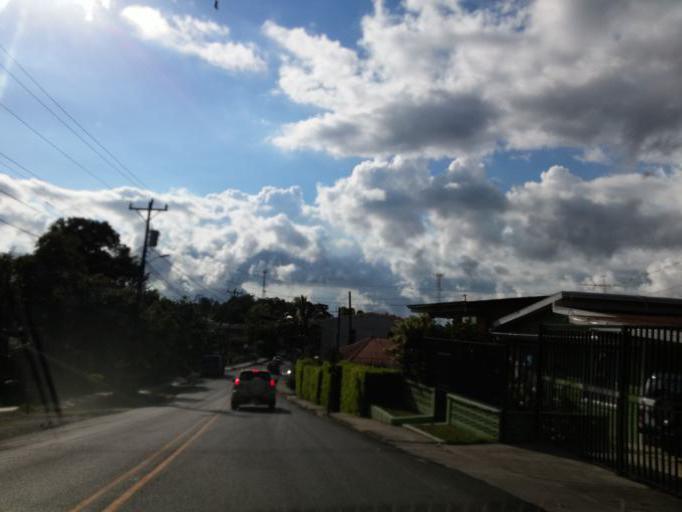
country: CR
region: San Jose
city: San Ignacio
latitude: 9.7966
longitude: -84.1284
